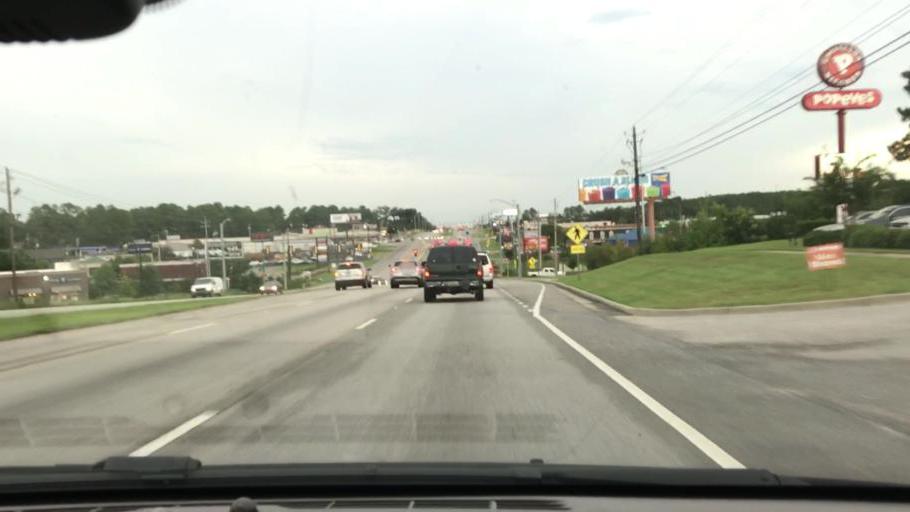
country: US
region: Alabama
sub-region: Houston County
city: Dothan
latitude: 31.2544
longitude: -85.4301
